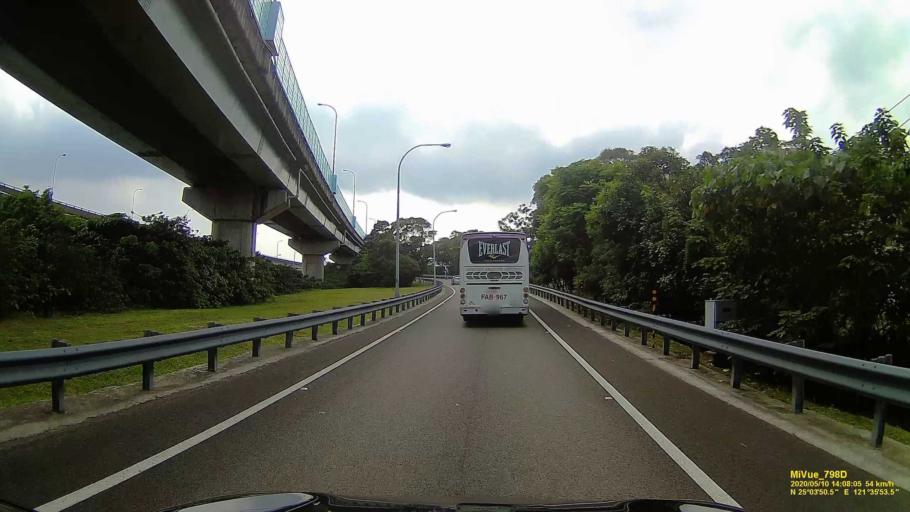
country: TW
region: Taipei
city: Taipei
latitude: 25.0641
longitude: 121.5979
